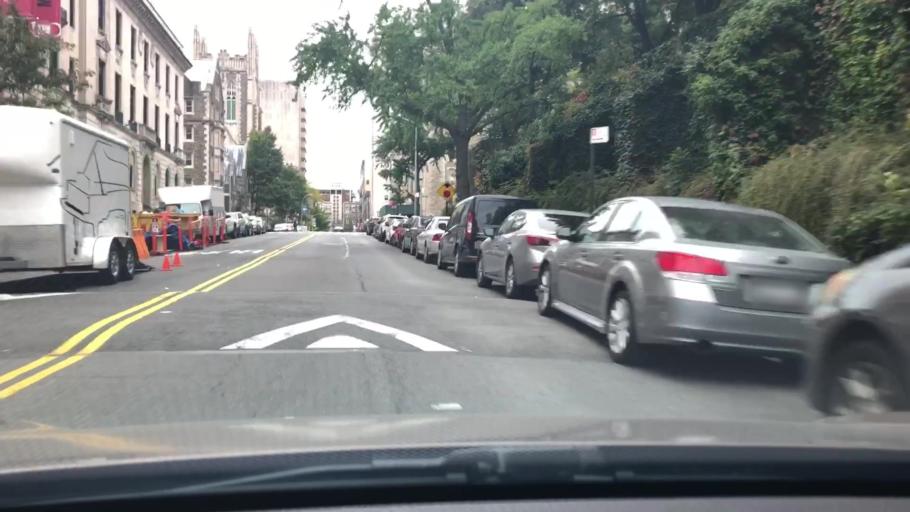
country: US
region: New Jersey
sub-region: Bergen County
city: Edgewater
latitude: 40.8131
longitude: -73.9616
